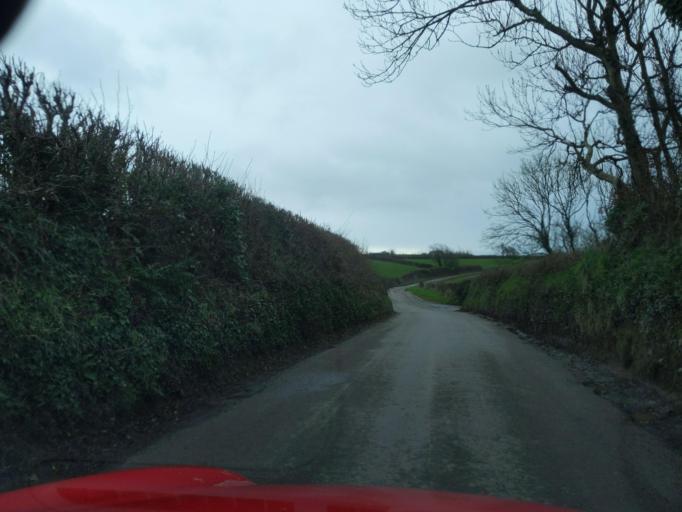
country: GB
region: England
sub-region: Devon
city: Modbury
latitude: 50.3360
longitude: -3.8687
